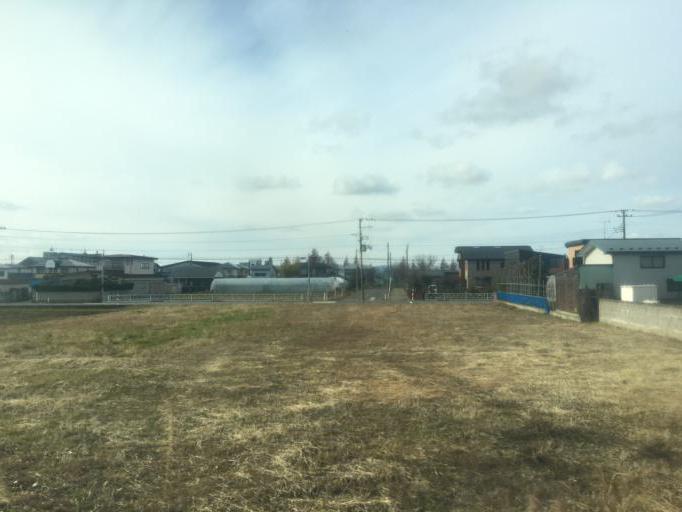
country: JP
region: Akita
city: Tenno
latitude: 39.9517
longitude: 140.0775
